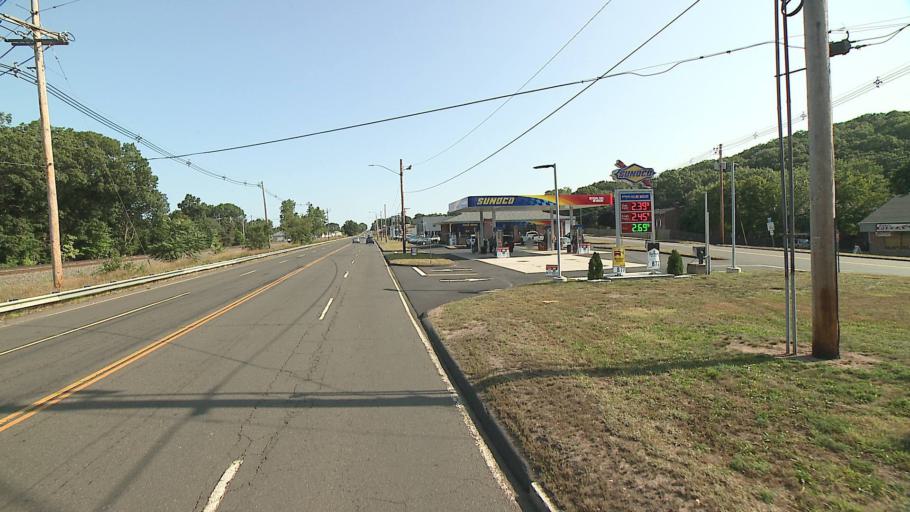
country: US
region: Connecticut
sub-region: New Haven County
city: Wallingford Center
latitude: 41.4382
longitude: -72.8330
